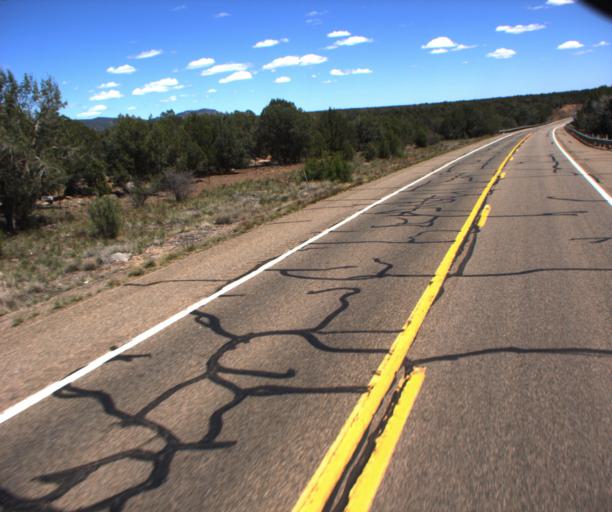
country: US
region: Arizona
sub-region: Yavapai County
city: Paulden
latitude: 35.0869
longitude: -112.4101
